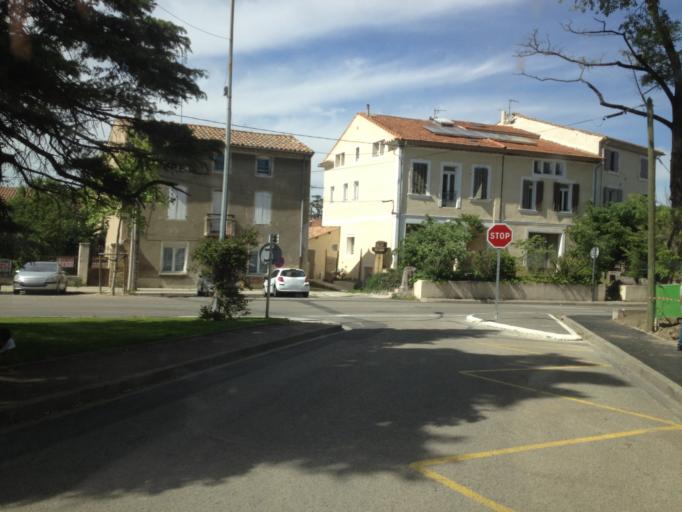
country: FR
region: Provence-Alpes-Cote d'Azur
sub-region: Departement du Vaucluse
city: Sorgues
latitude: 44.0055
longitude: 4.8753
